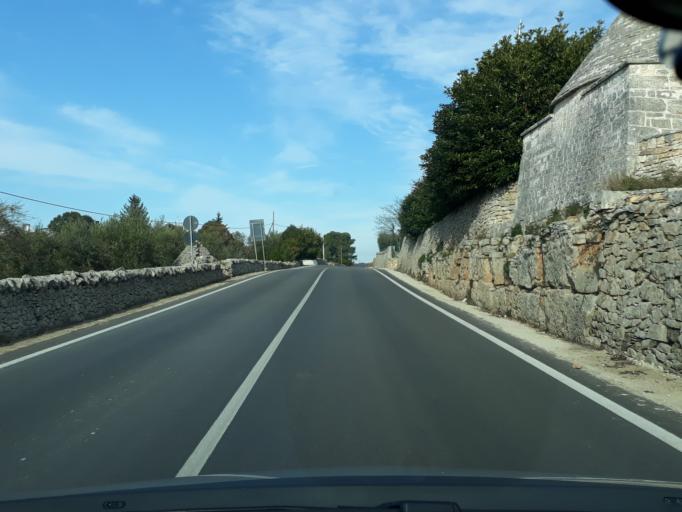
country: IT
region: Apulia
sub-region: Provincia di Bari
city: Locorotondo
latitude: 40.7674
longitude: 17.3330
